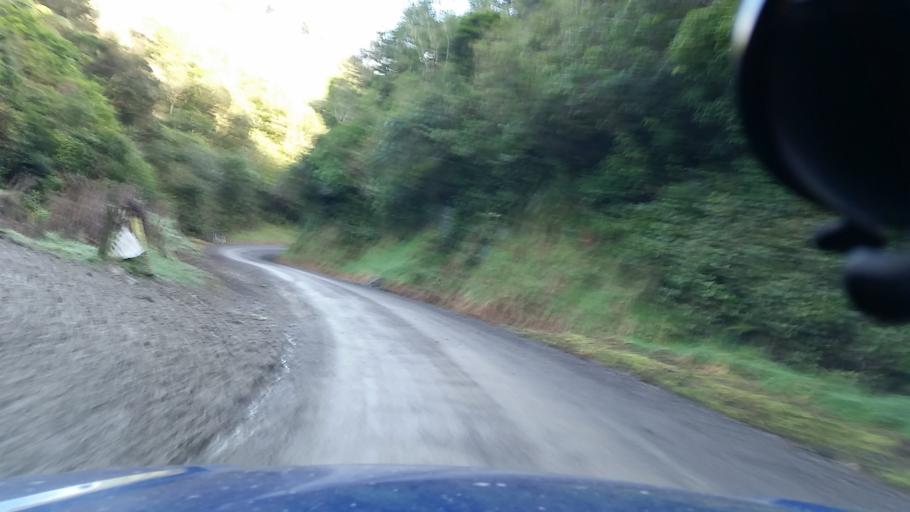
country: NZ
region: Taranaki
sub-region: New Plymouth District
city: Waitara
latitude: -39.0614
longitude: 174.7873
